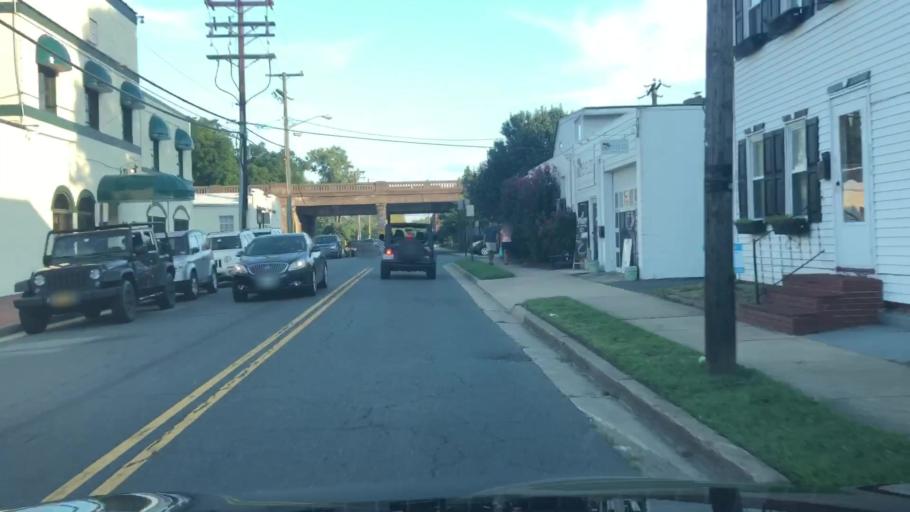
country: US
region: Virginia
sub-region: City of Fredericksburg
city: Fredericksburg
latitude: 38.2995
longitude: -77.4557
